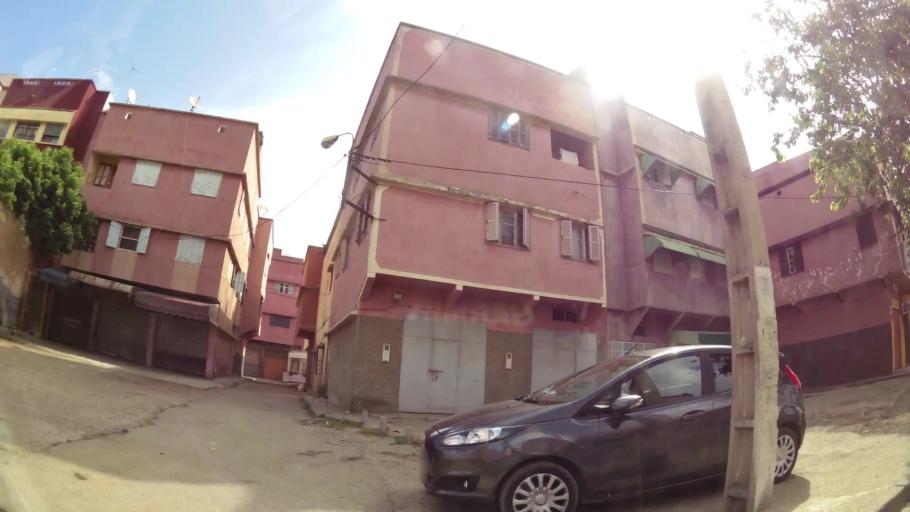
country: MA
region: Gharb-Chrarda-Beni Hssen
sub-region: Kenitra Province
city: Kenitra
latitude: 34.2705
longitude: -6.5625
